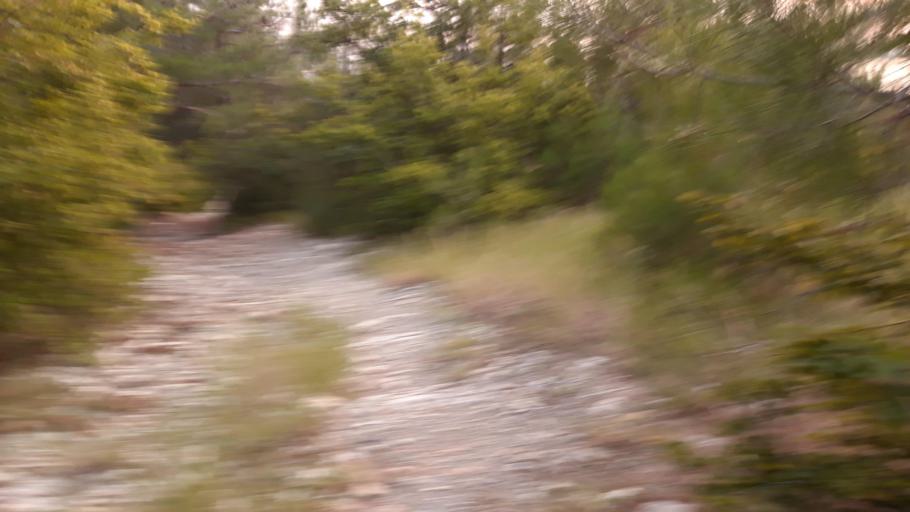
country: RU
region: Krasnodarskiy
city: Gelendzhik
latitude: 44.5811
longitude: 38.0848
